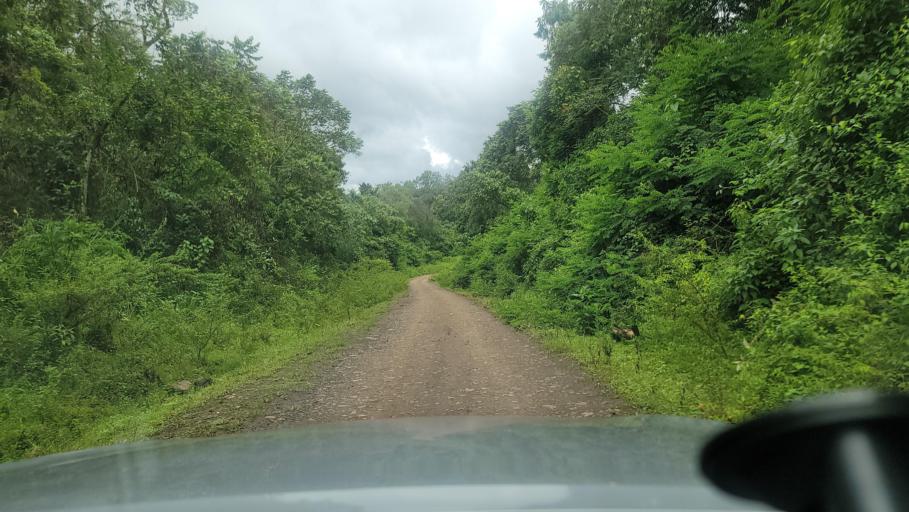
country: ET
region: Southern Nations, Nationalities, and People's Region
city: Bonga
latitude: 7.6384
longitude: 36.2318
